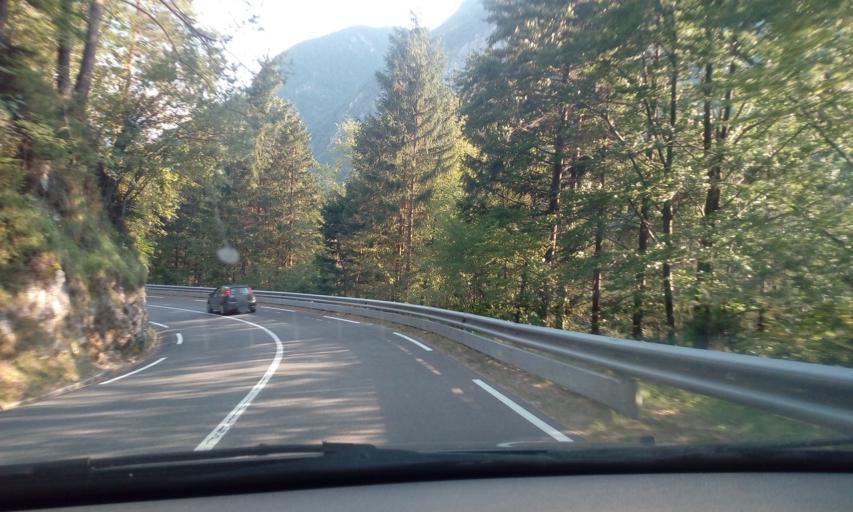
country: SI
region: Bovec
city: Bovec
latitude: 46.3819
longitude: 13.5844
